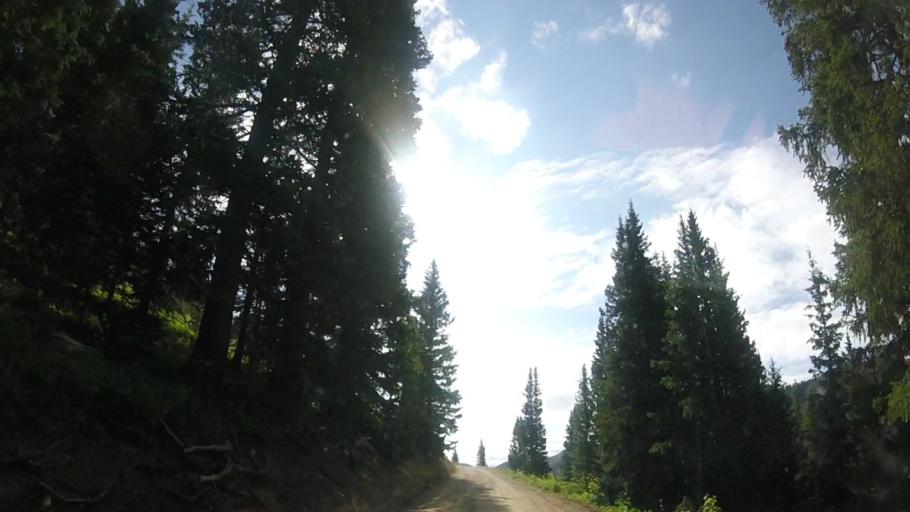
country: US
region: Colorado
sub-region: San Miguel County
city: Telluride
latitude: 37.8469
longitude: -107.7685
